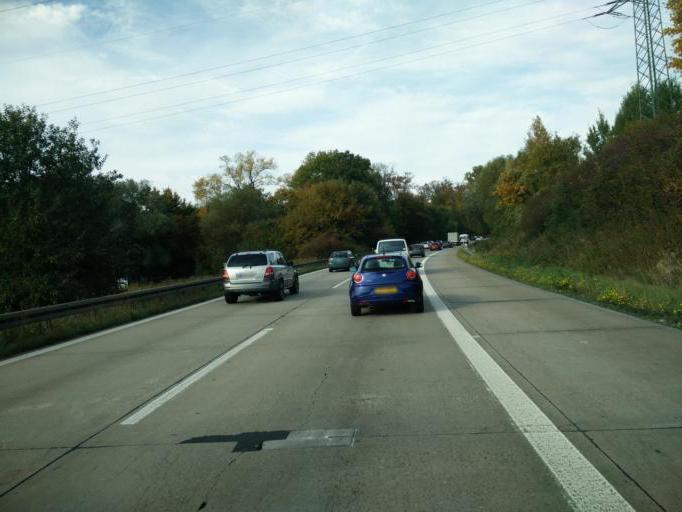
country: DE
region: Baden-Wuerttemberg
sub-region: Karlsruhe Region
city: Ettlingen
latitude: 48.9731
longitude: 8.4405
